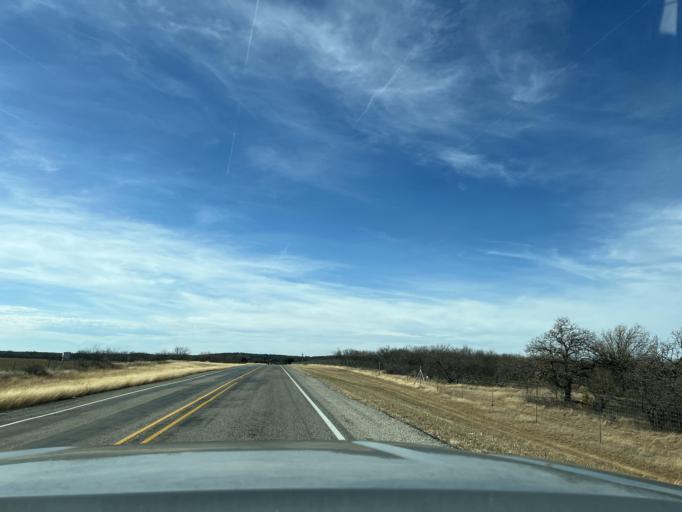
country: US
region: Texas
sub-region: Eastland County
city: Cisco
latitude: 32.4595
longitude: -98.9951
